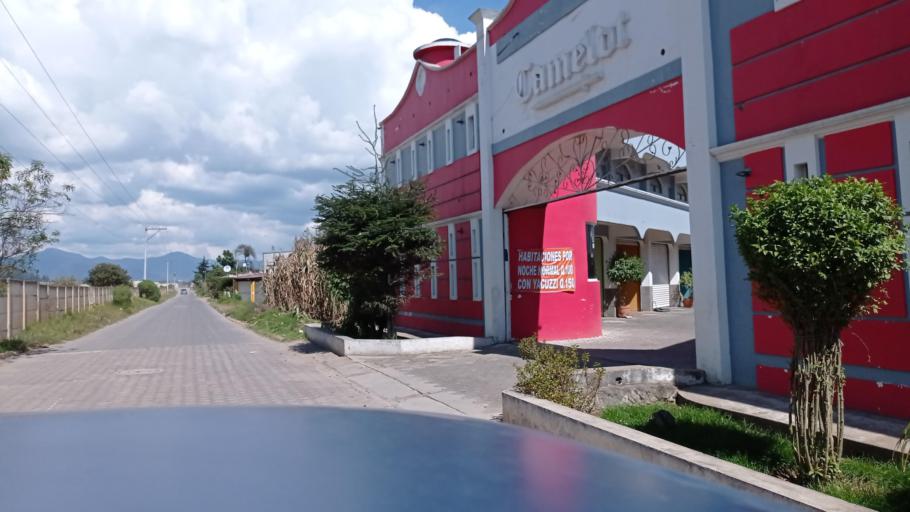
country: GT
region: Quetzaltenango
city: Olintepeque
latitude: 14.8686
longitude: -91.4958
